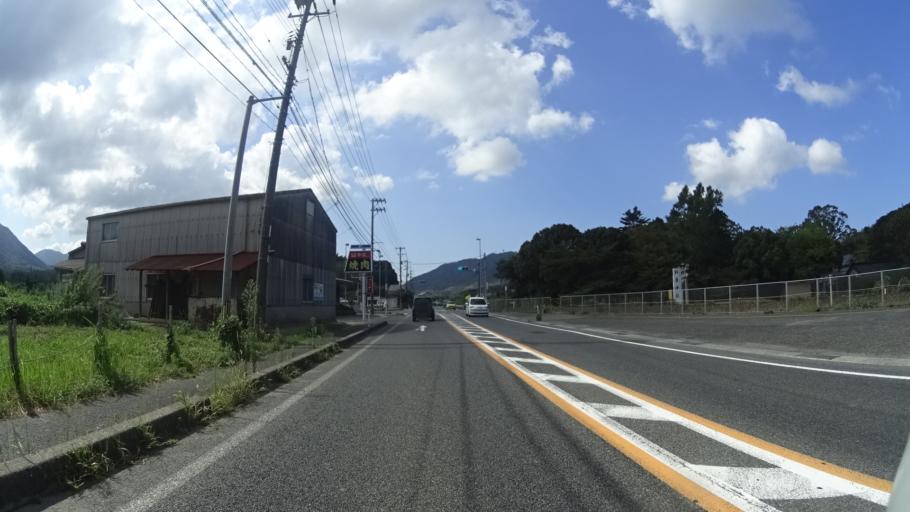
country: JP
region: Yamaguchi
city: Shimonoseki
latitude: 34.1233
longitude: 130.9123
